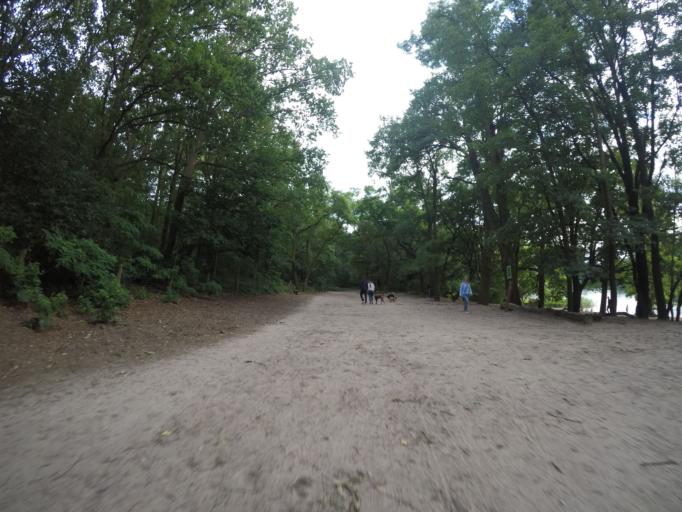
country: DE
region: Berlin
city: Grunewald
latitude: 52.4705
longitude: 13.2651
